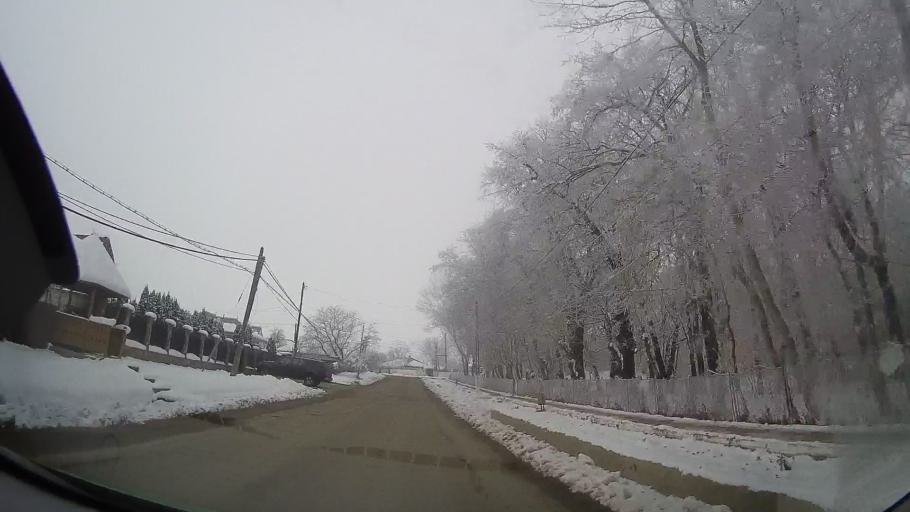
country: RO
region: Iasi
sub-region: Comuna Tibanesti
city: Tibanesti
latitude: 46.9071
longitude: 27.3370
